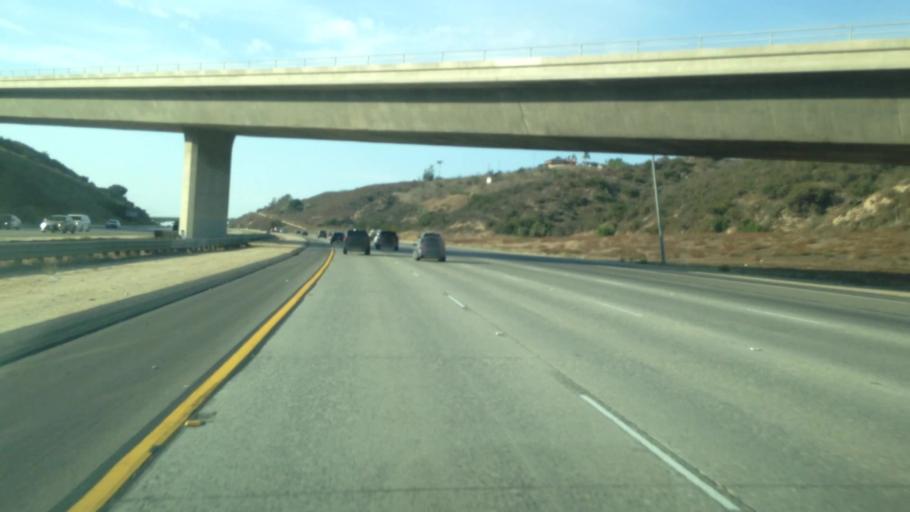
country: US
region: California
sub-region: San Diego County
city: Hidden Meadows
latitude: 33.2858
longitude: -117.1495
